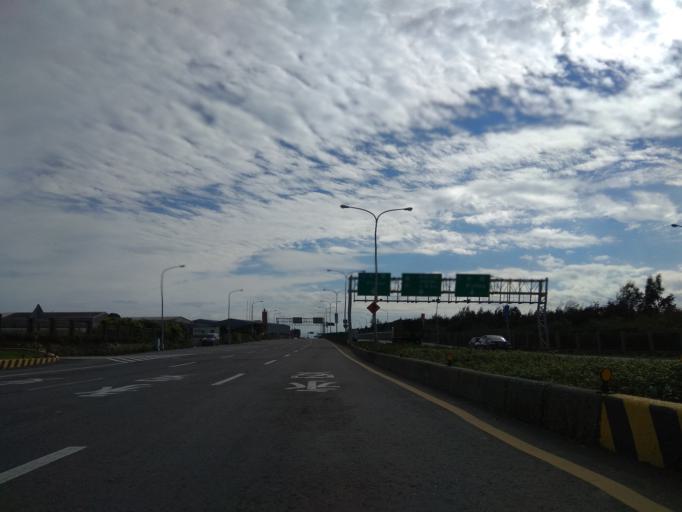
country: TW
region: Taiwan
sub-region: Hsinchu
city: Zhubei
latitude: 25.0291
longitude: 121.0543
